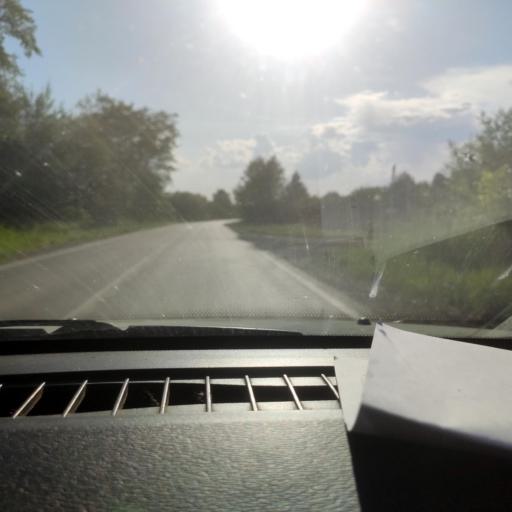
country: RU
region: Perm
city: Krasnokamsk
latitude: 58.1337
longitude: 55.7515
